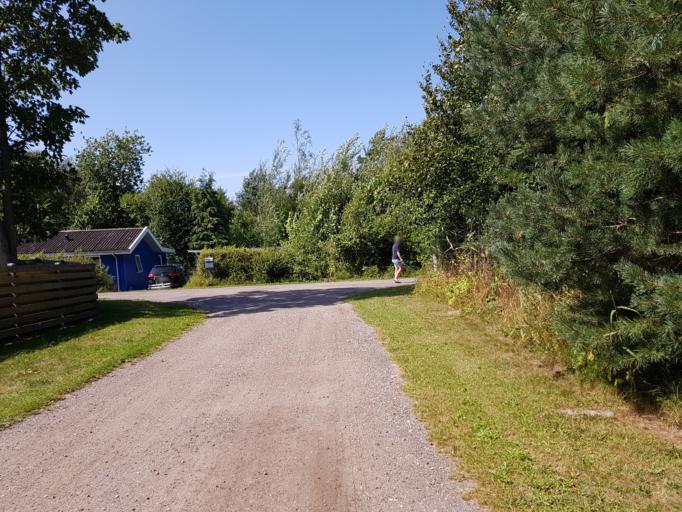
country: DK
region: Zealand
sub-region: Guldborgsund Kommune
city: Nykobing Falster
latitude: 54.6044
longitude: 11.9516
